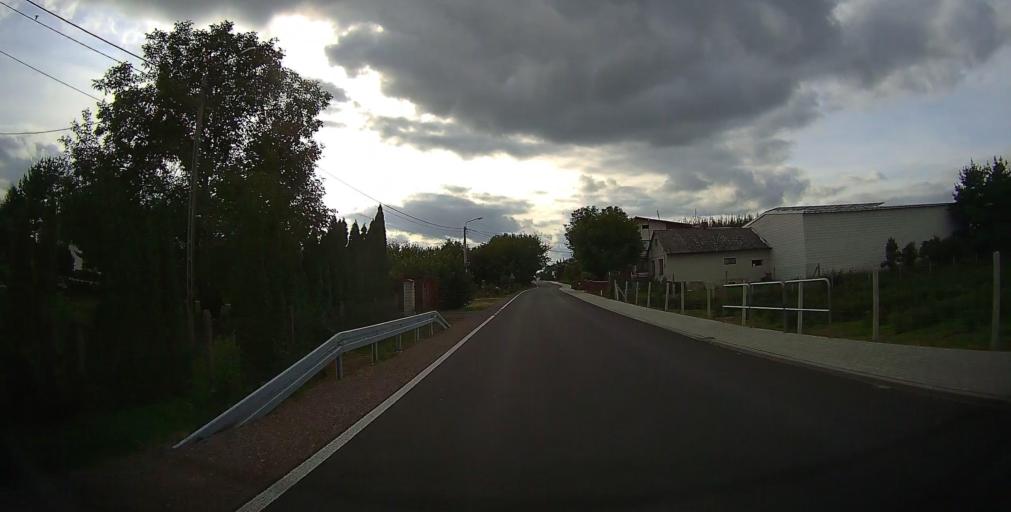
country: PL
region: Masovian Voivodeship
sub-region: Powiat bialobrzeski
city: Promna
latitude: 51.7086
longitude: 20.9533
